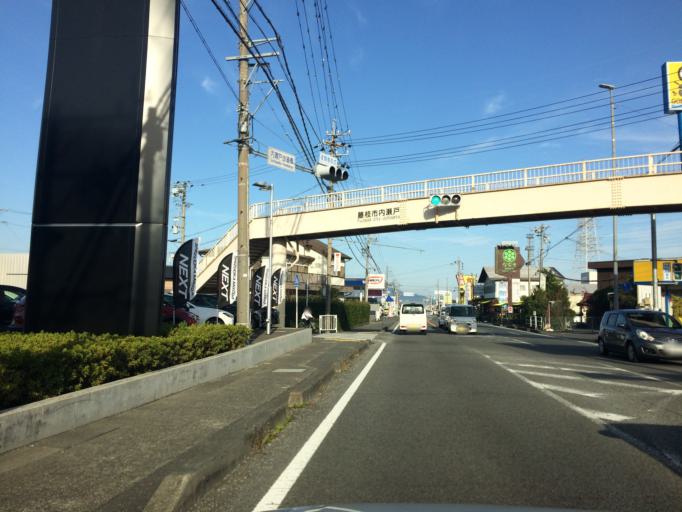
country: JP
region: Shizuoka
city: Fujieda
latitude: 34.8472
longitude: 138.2324
